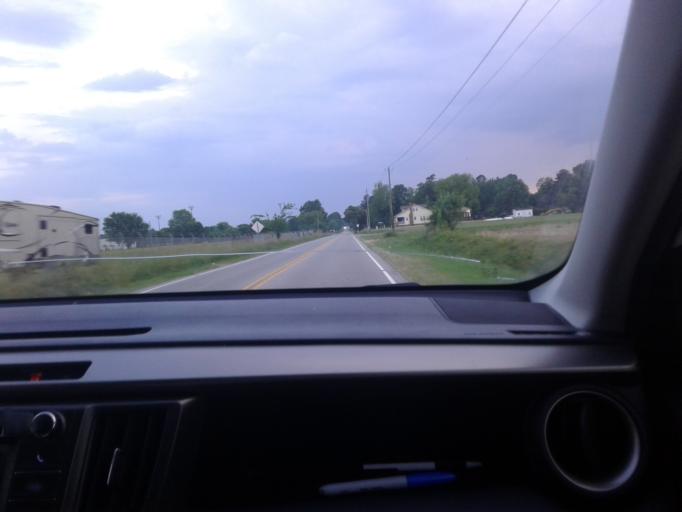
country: US
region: North Carolina
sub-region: Harnett County
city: Dunn
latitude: 35.3296
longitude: -78.5957
